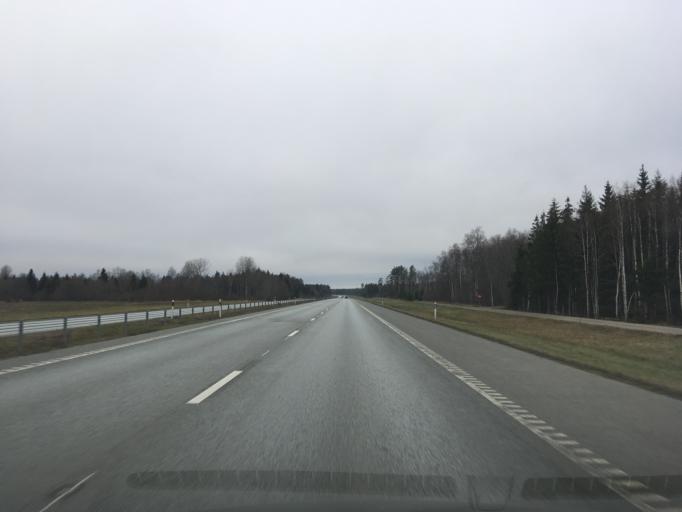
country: EE
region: Laeaene-Virumaa
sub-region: Kadrina vald
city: Kadrina
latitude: 59.4529
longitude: 26.0582
